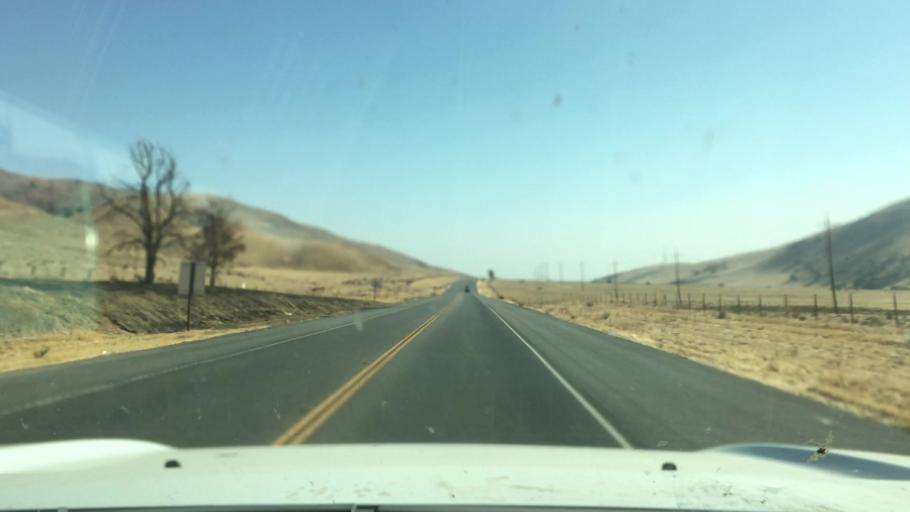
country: US
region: California
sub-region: San Luis Obispo County
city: Shandon
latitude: 35.7299
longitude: -120.2025
